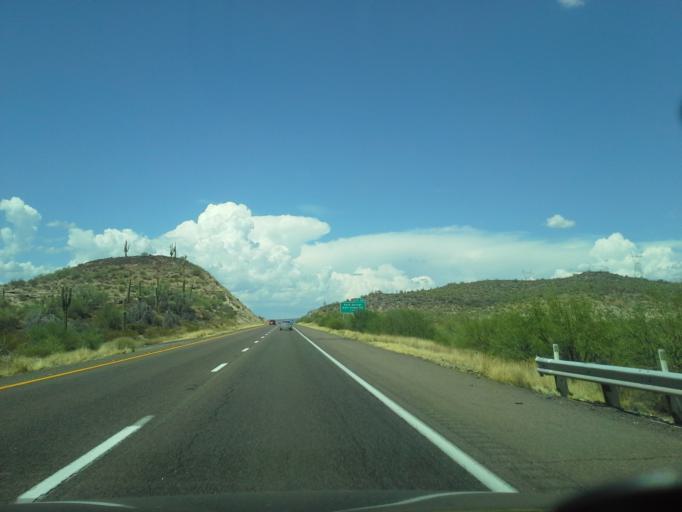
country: US
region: Arizona
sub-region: Yavapai County
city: Black Canyon City
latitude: 34.0329
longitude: -112.1455
